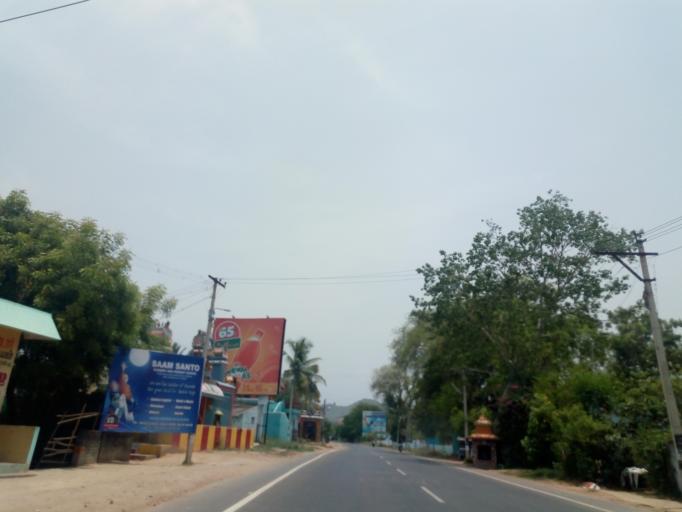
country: IN
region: Tamil Nadu
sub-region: Vellore
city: Vellore
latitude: 12.8734
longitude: 79.1003
